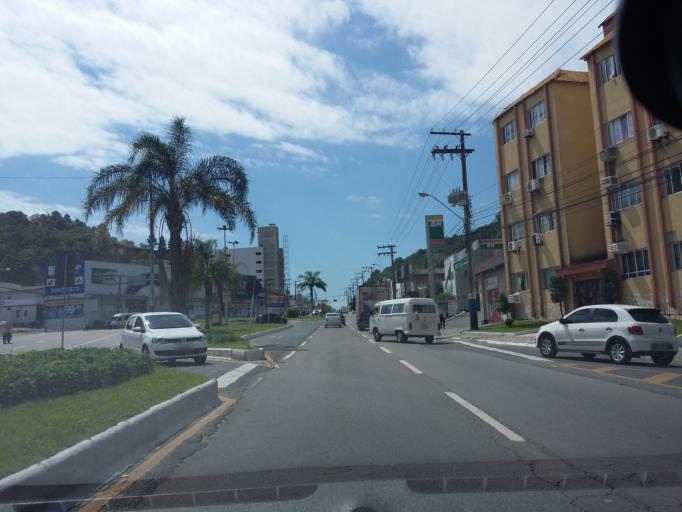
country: BR
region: Santa Catarina
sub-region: Balneario Camboriu
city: Balneario Camboriu
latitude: -26.9681
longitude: -48.6393
